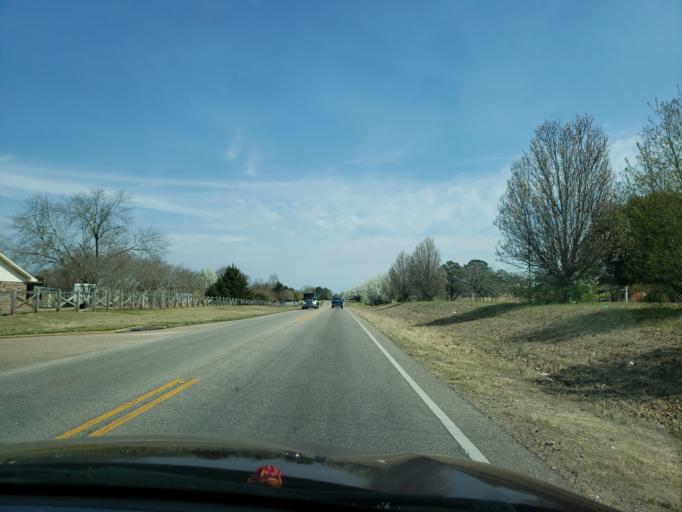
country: US
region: Alabama
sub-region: Elmore County
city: Coosada
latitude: 32.5272
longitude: -86.3557
